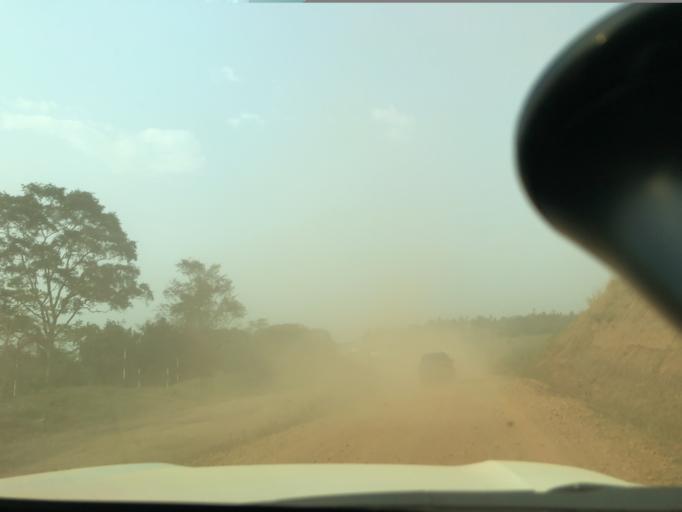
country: CD
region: Nord Kivu
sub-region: North Kivu
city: Butembo
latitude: 0.1229
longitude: 29.6400
